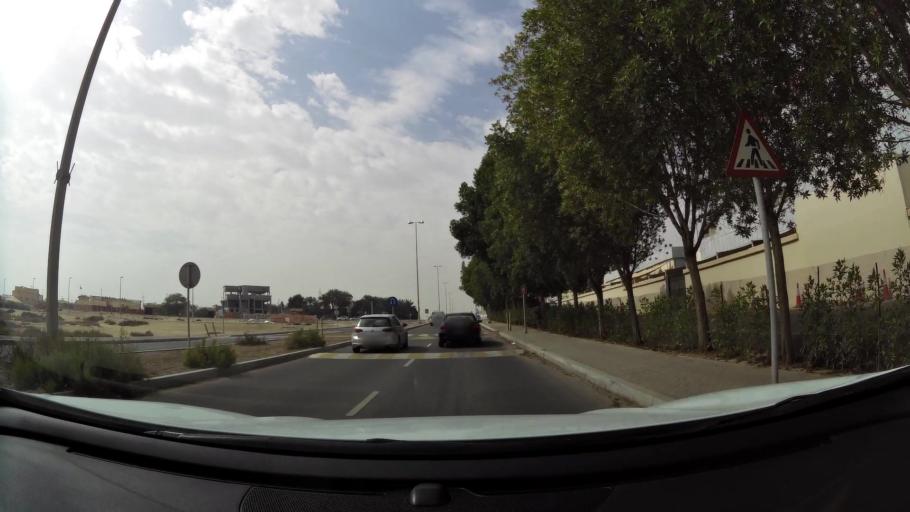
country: AE
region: Abu Dhabi
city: Abu Dhabi
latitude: 24.3236
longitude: 54.6339
